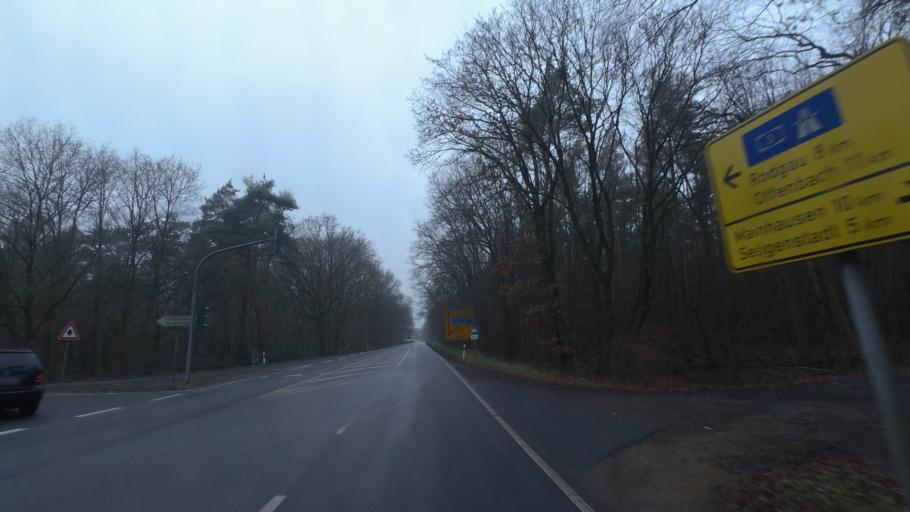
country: DE
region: Hesse
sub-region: Regierungsbezirk Darmstadt
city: Rodgau
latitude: 50.0603
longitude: 8.8991
